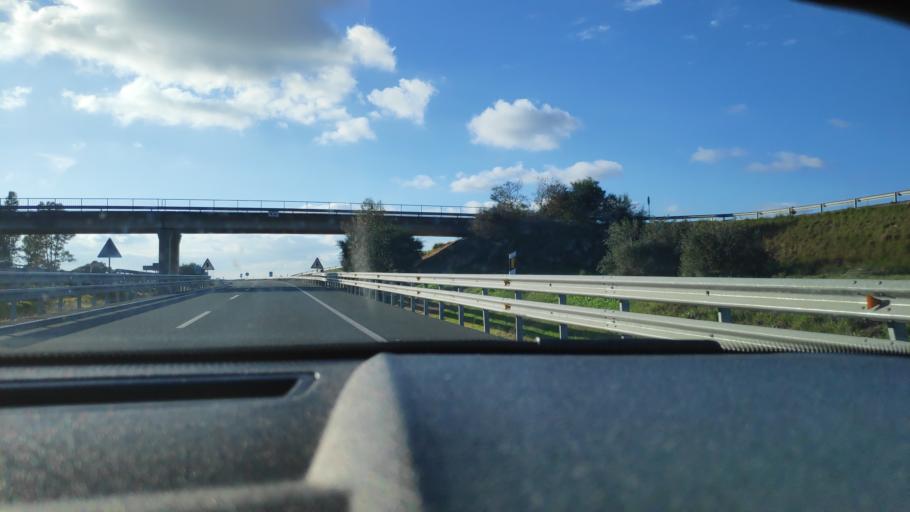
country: ES
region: Andalusia
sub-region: Provincia de Sevilla
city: Fuentes de Andalucia
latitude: 37.5103
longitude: -5.3556
